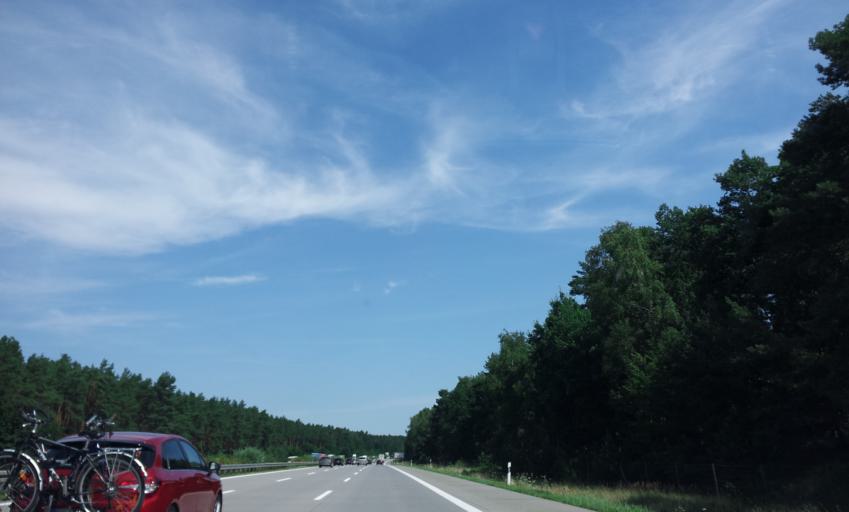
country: DE
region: Brandenburg
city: Erkner
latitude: 52.3585
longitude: 13.7602
